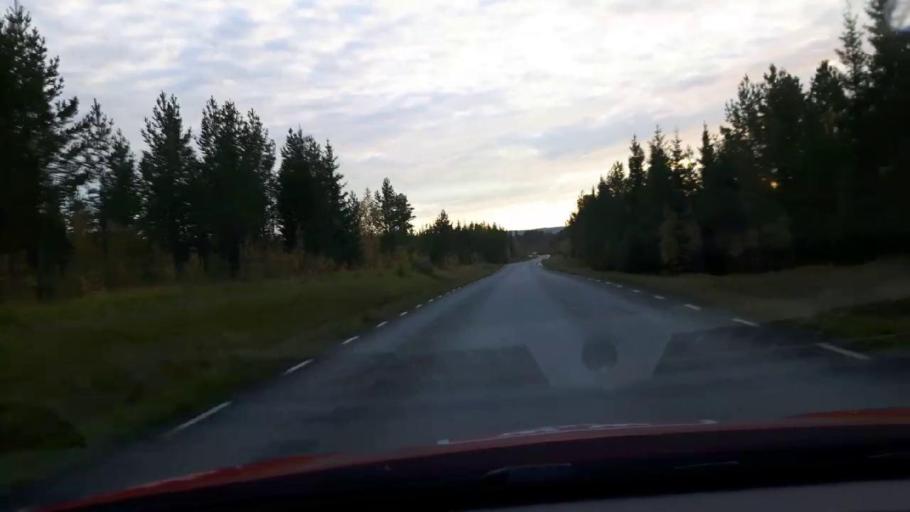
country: SE
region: Jaemtland
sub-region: OEstersunds Kommun
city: Lit
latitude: 63.3132
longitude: 15.0211
